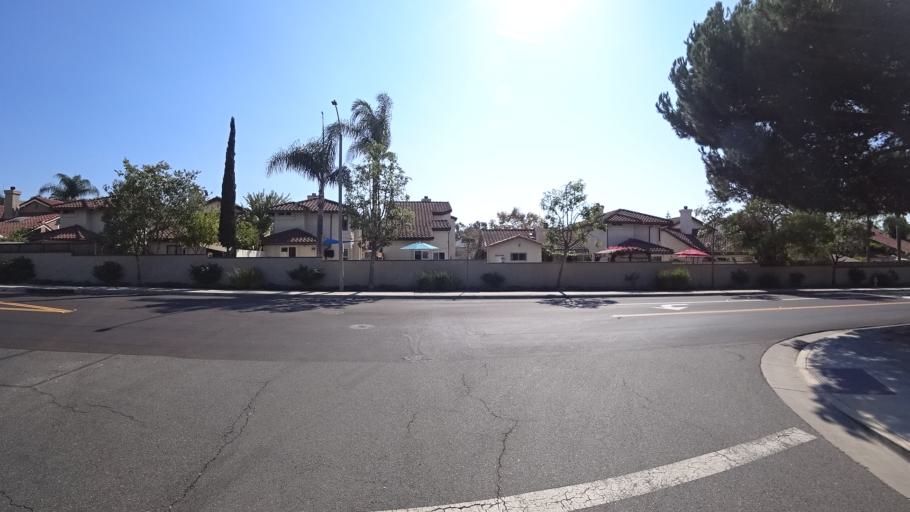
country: US
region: California
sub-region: Orange County
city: San Juan Capistrano
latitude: 33.4719
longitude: -117.6362
